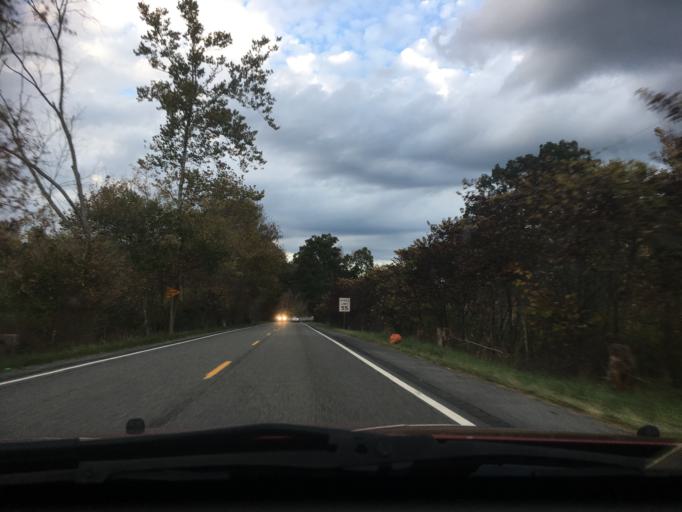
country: US
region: Virginia
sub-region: Pulaski County
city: Dublin
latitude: 37.2034
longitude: -80.7371
